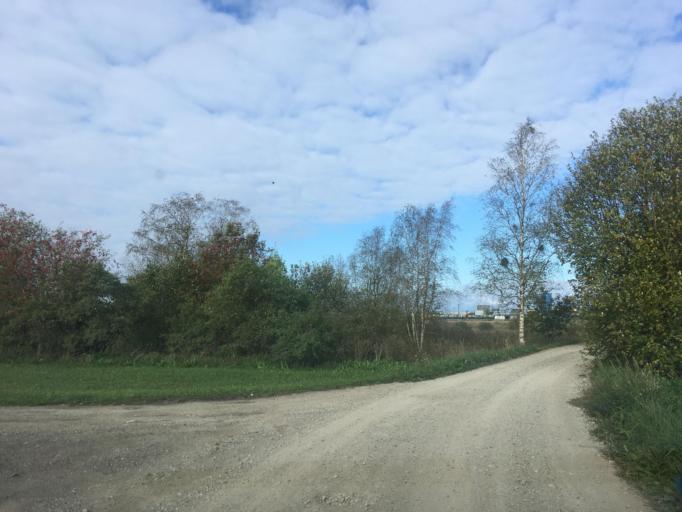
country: EE
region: Harju
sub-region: Joelaehtme vald
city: Loo
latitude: 59.4471
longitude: 24.9676
